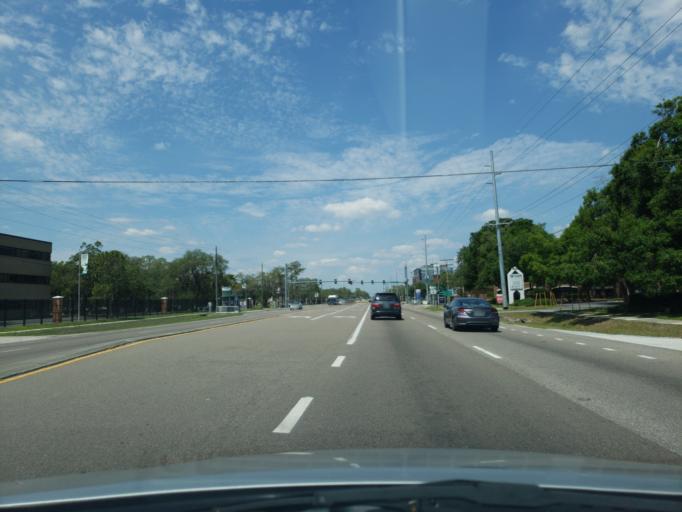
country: US
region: Florida
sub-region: Hillsborough County
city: University
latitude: 28.0692
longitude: -82.4189
